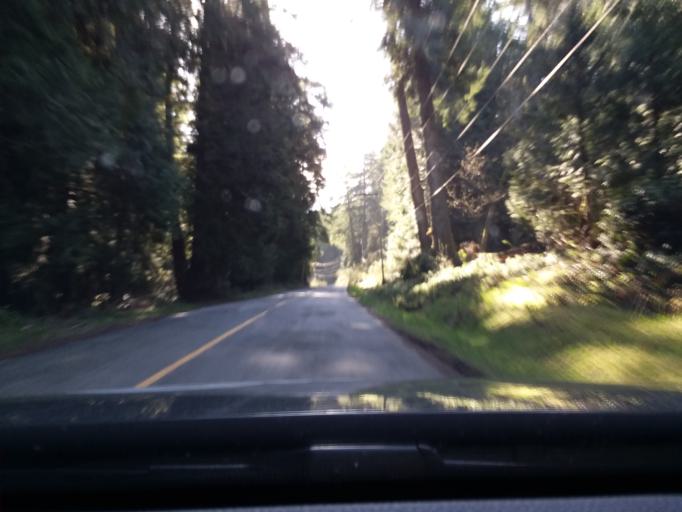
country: CA
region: British Columbia
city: North Cowichan
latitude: 48.9364
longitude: -123.4854
